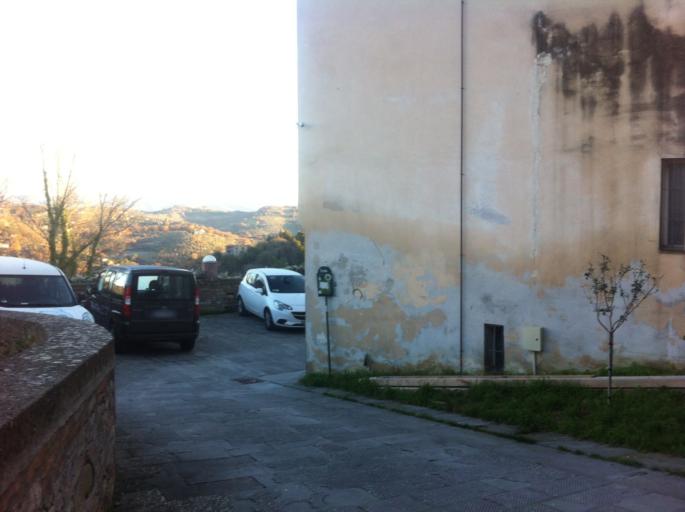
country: IT
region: Umbria
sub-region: Provincia di Perugia
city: Perugia
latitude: 43.1145
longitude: 12.3921
